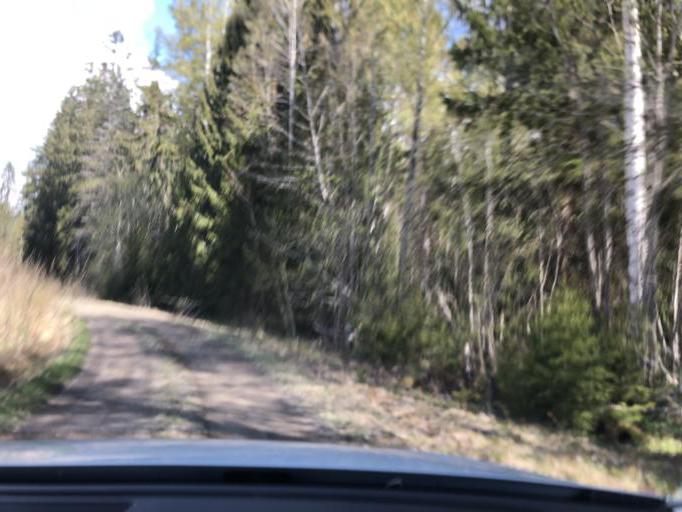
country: SE
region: Dalarna
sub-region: Avesta Kommun
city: Horndal
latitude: 60.2255
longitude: 16.5922
